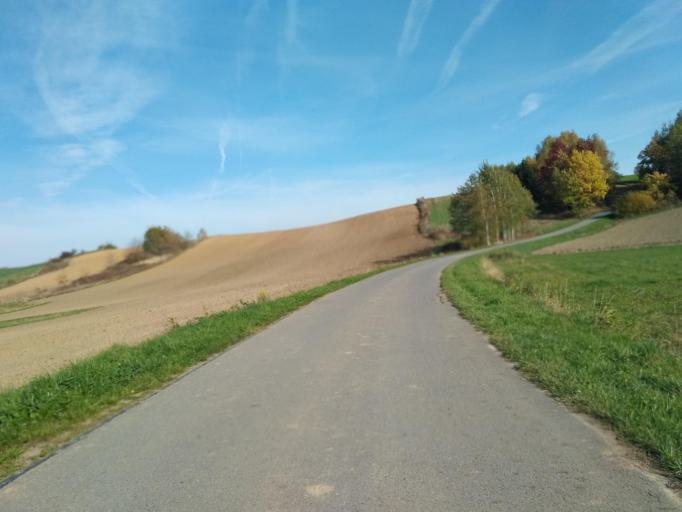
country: PL
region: Subcarpathian Voivodeship
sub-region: Powiat ropczycko-sedziszowski
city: Iwierzyce
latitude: 50.0498
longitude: 21.7543
